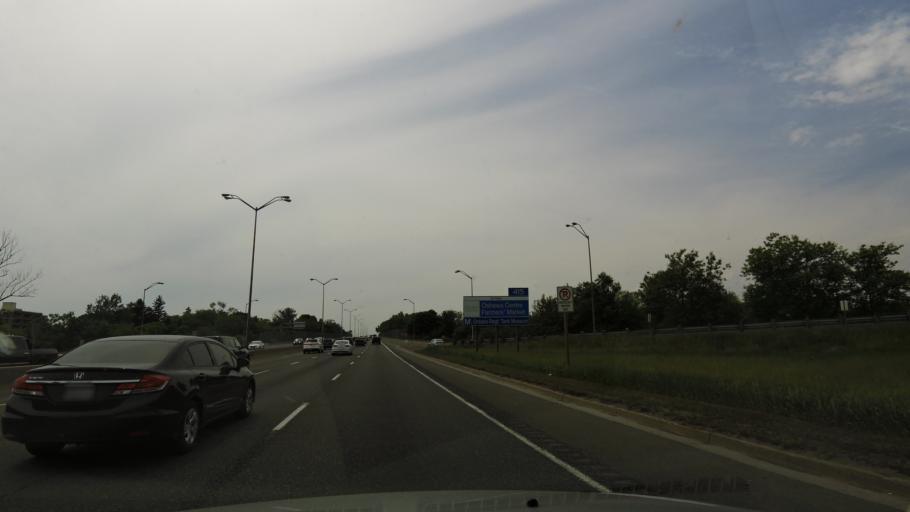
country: CA
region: Ontario
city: Oshawa
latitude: 43.8814
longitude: -78.8568
